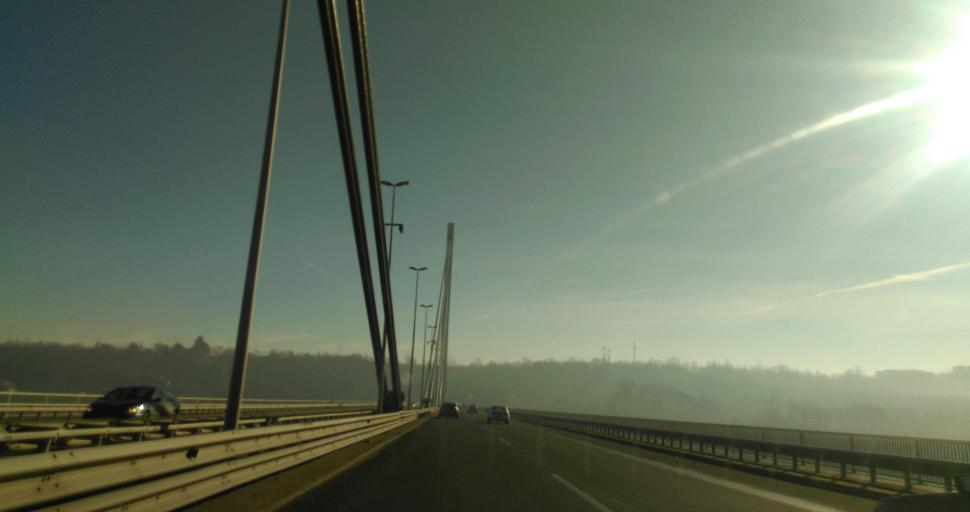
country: RS
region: Autonomna Pokrajina Vojvodina
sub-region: Juznobacki Okrug
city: Novi Sad
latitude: 45.2340
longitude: 19.8495
